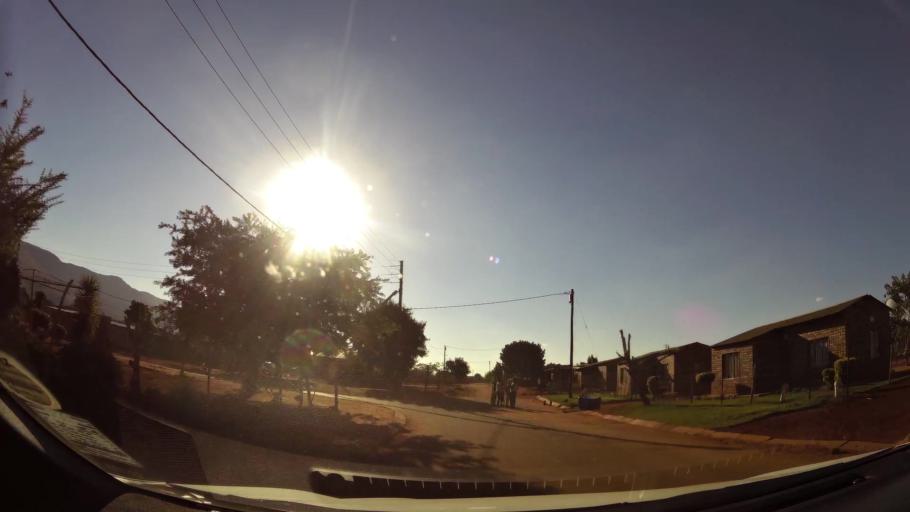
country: ZA
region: Limpopo
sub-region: Waterberg District Municipality
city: Mokopane
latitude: -24.1870
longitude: 28.9741
